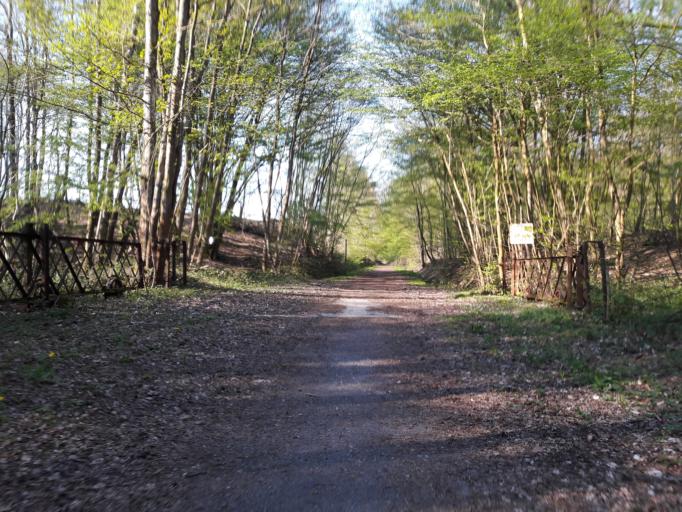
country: FR
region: Nord-Pas-de-Calais
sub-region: Departement du Nord
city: Sains-du-Nord
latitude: 50.1391
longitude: 4.0665
